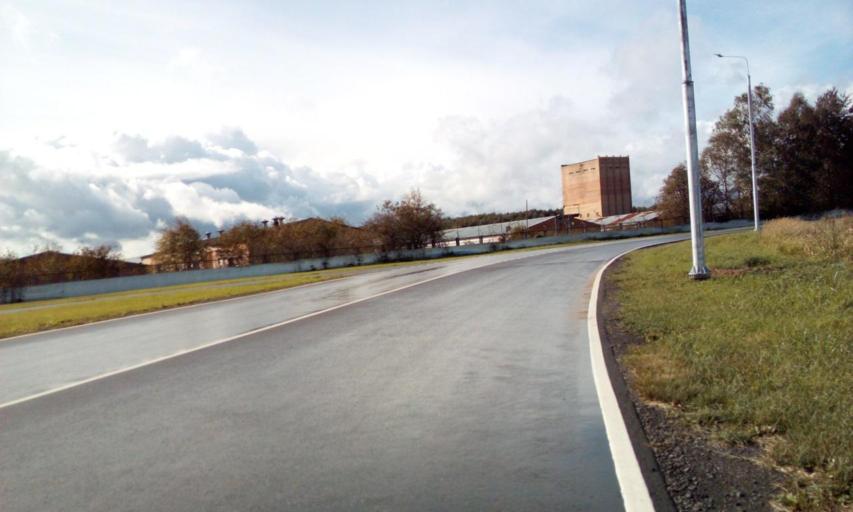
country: RU
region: Moskovskaya
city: Kievskij
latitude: 55.4361
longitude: 36.9145
